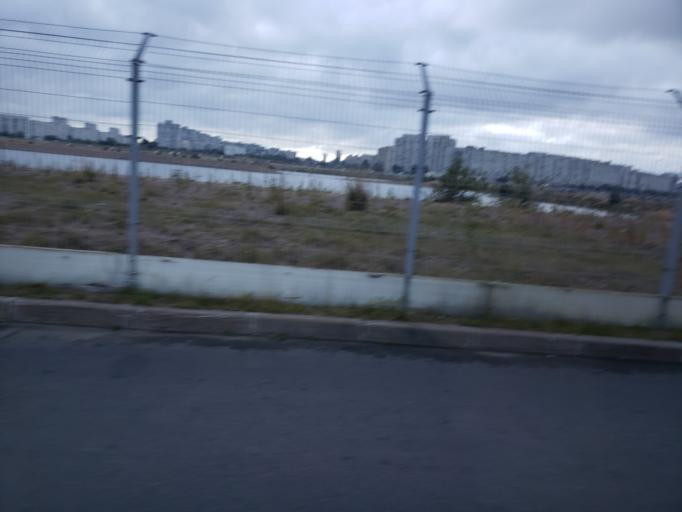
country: RU
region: St.-Petersburg
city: Vasyl'evsky Ostrov
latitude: 59.9491
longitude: 30.1963
